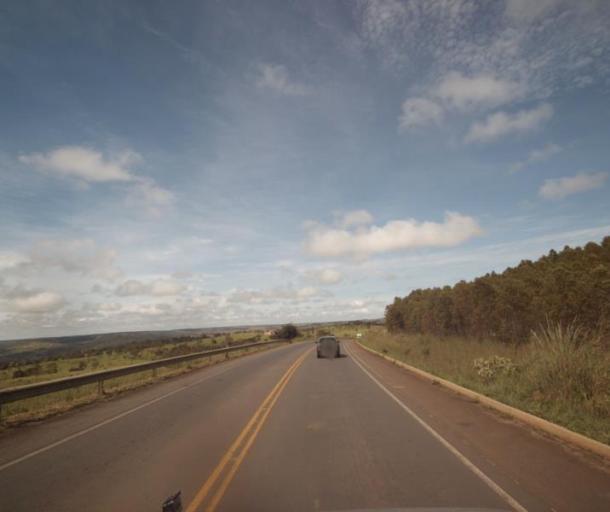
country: BR
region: Goias
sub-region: Abadiania
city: Abadiania
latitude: -16.0913
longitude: -48.8524
